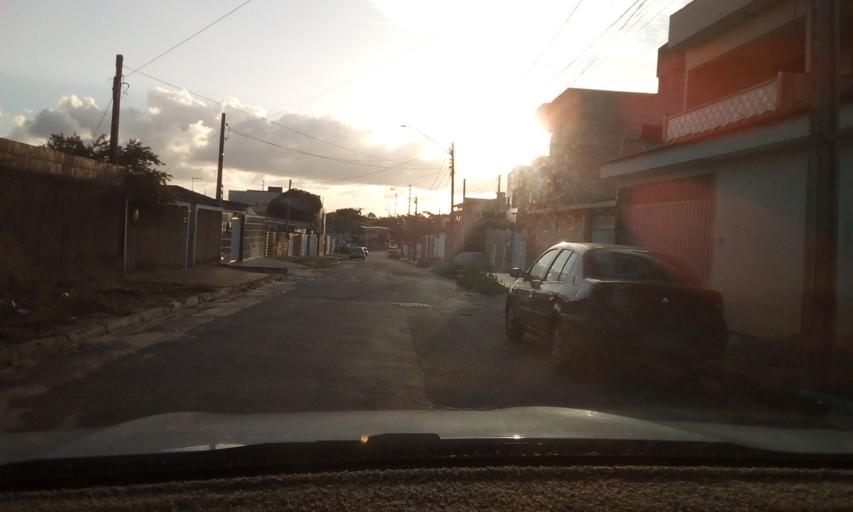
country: BR
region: Paraiba
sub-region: Joao Pessoa
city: Joao Pessoa
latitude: -7.1728
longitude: -34.8850
